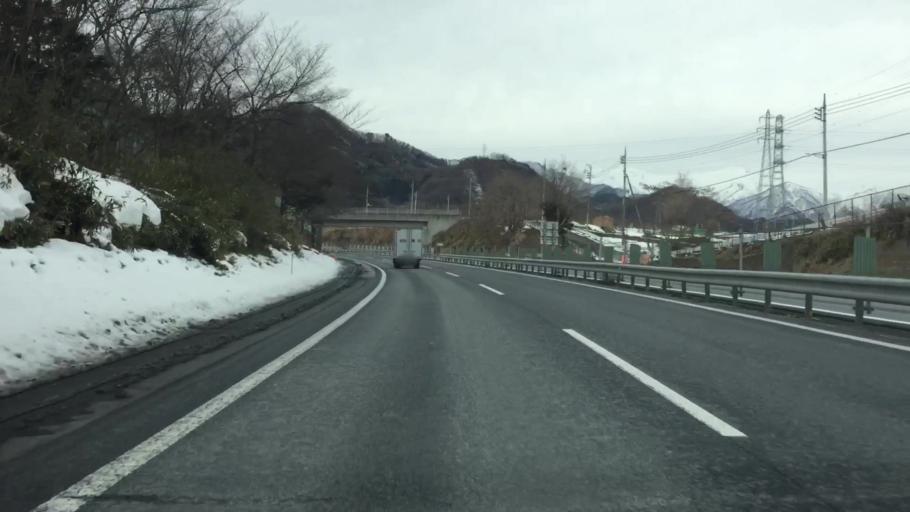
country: JP
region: Gunma
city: Numata
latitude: 36.7074
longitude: 138.9834
